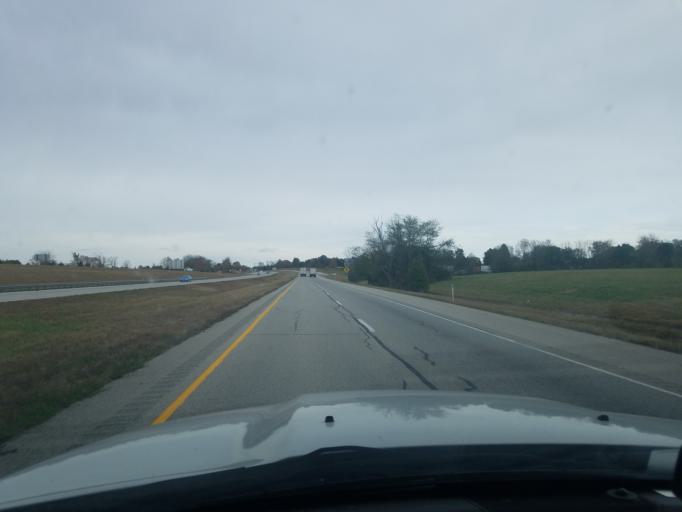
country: US
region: Indiana
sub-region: Crawford County
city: English
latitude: 38.2424
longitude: -86.3597
